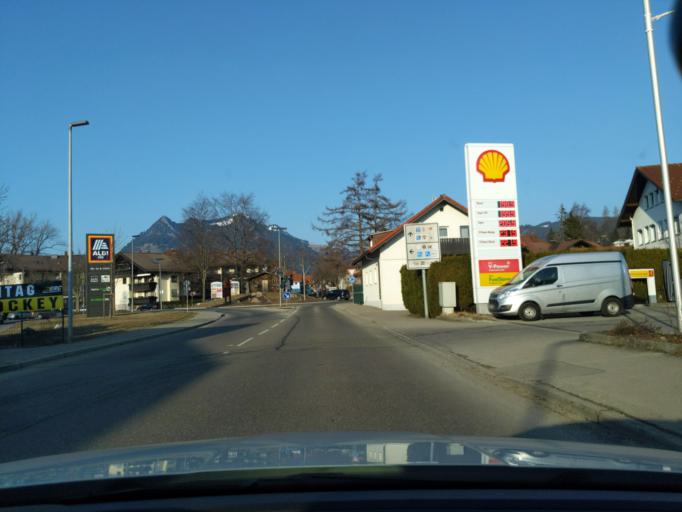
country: DE
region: Bavaria
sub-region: Swabia
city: Sonthofen
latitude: 47.5080
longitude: 10.2756
